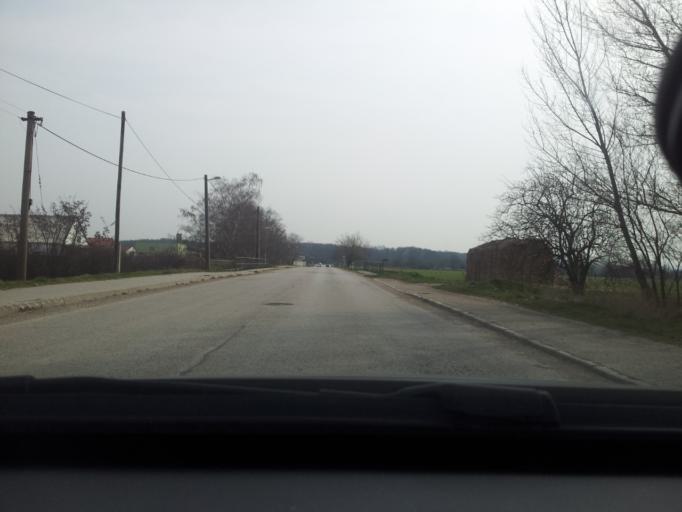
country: SK
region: Trnavsky
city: Leopoldov
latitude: 48.4569
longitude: 17.7225
